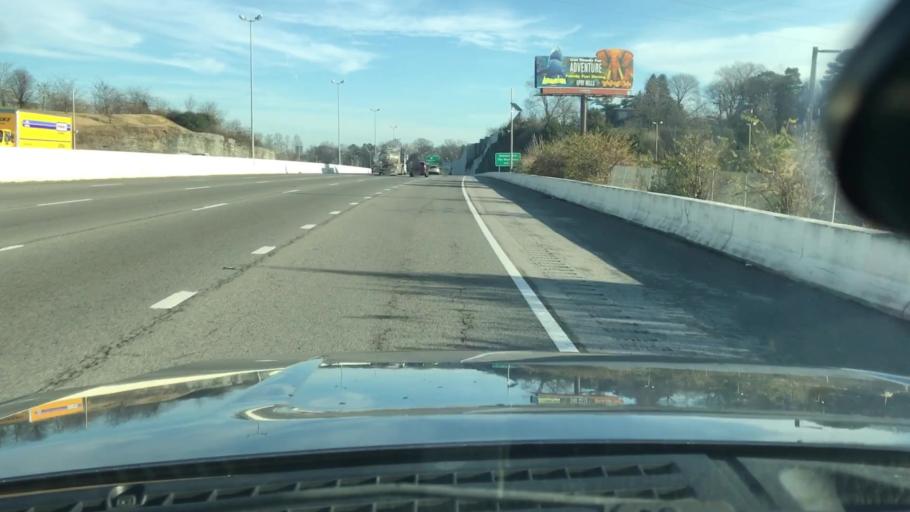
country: US
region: Tennessee
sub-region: Davidson County
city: Nashville
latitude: 36.1616
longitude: -86.6908
